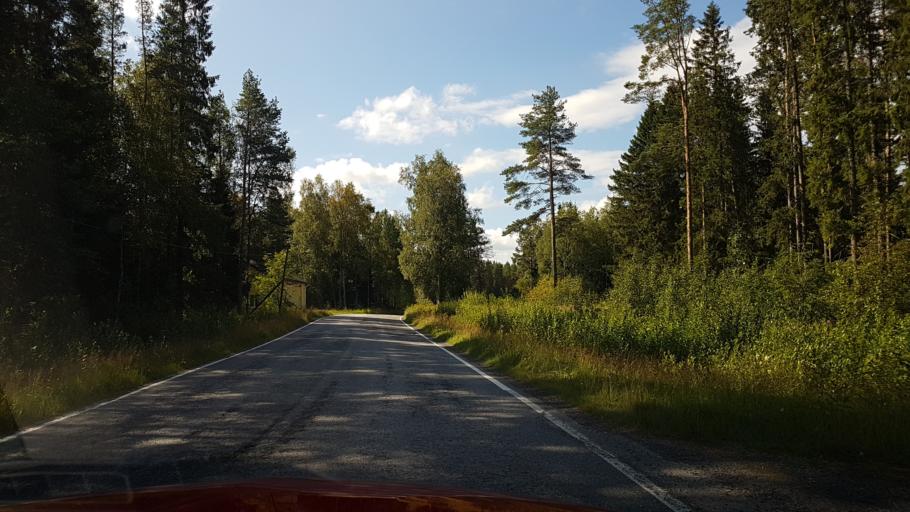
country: FI
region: Northern Ostrobothnia
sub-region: Ylivieska
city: Himanka
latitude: 64.0924
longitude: 23.7643
